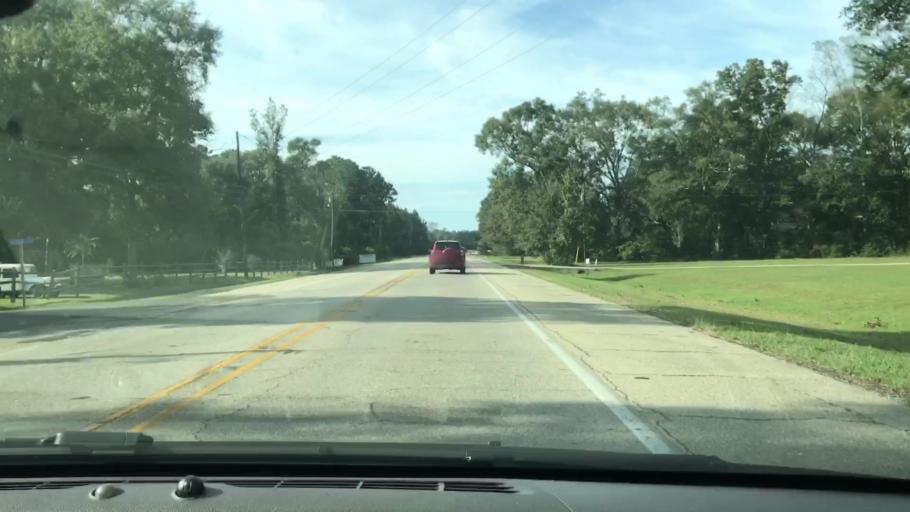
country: US
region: Louisiana
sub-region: Saint Tammany Parish
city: Pearl River
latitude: 30.4608
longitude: -89.8064
